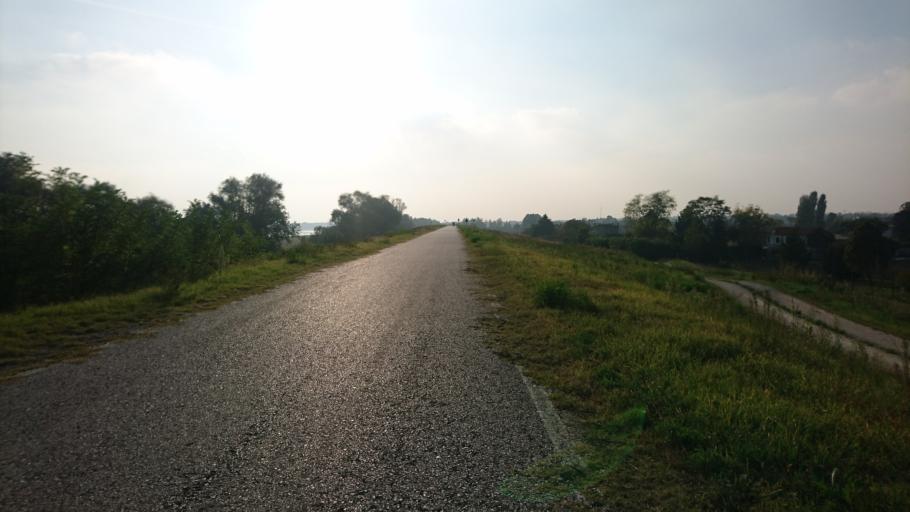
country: IT
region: Veneto
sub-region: Provincia di Rovigo
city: Canaro
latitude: 44.9284
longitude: 11.7146
